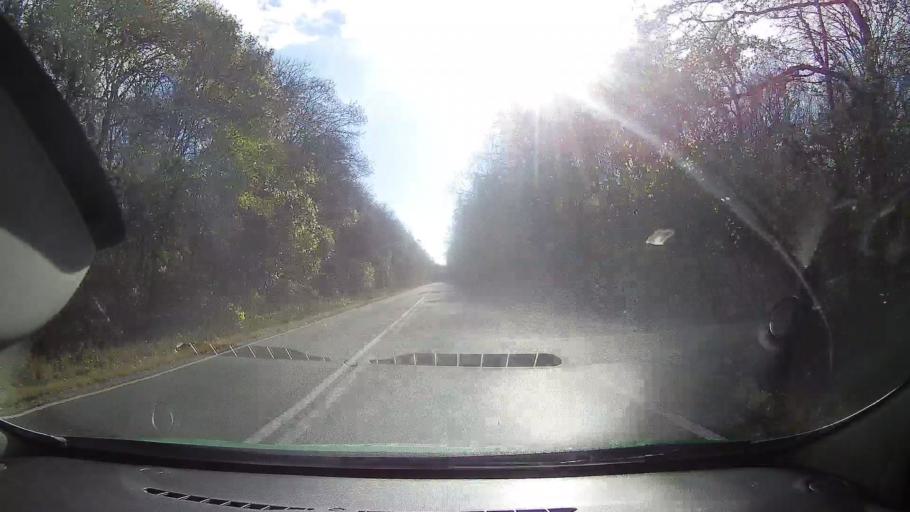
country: RO
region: Tulcea
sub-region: Oras Babadag
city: Babadag
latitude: 44.8489
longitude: 28.6981
